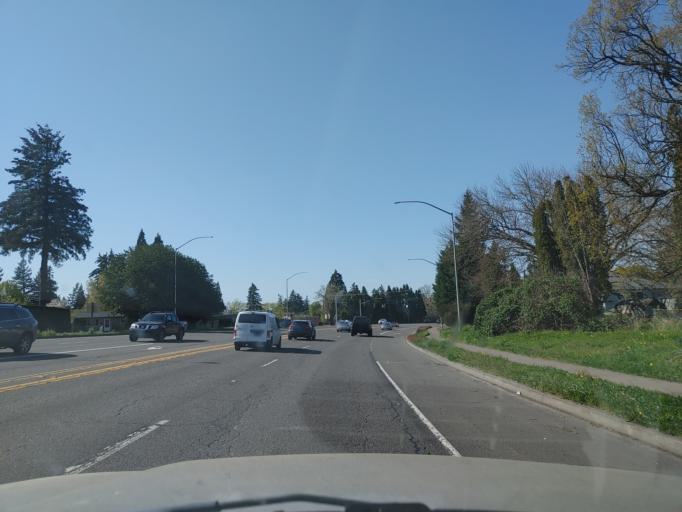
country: US
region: Oregon
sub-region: Clackamas County
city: Milwaukie
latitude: 45.4440
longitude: -122.6306
